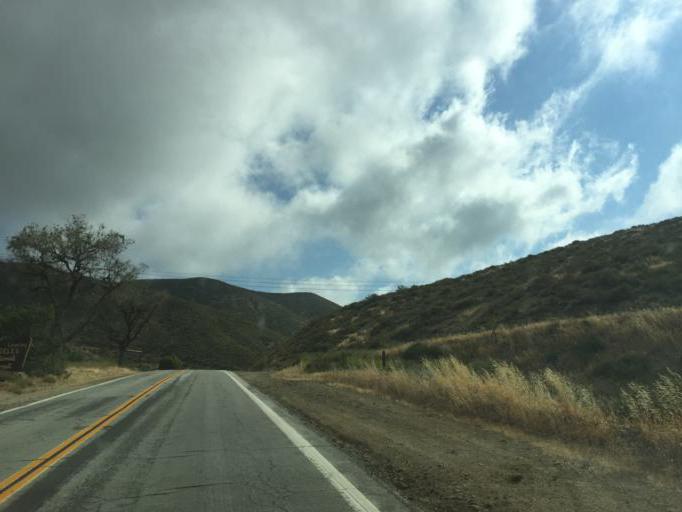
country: US
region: California
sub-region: Los Angeles County
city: Leona Valley
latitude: 34.5860
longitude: -118.3058
